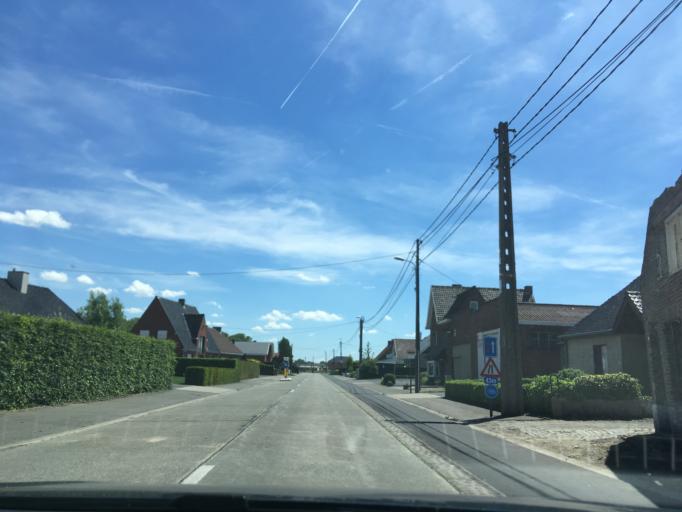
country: BE
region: Flanders
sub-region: Provincie West-Vlaanderen
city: Hooglede
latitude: 51.0107
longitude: 3.0815
